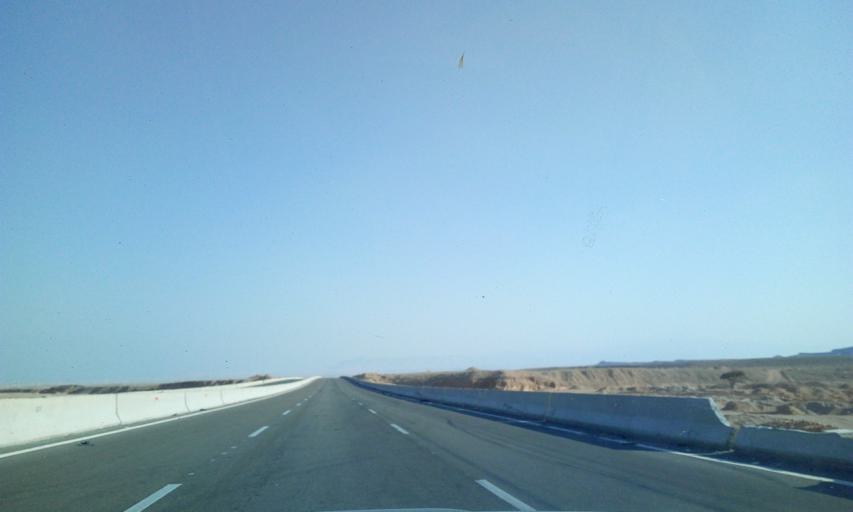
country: EG
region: As Suways
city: Ain Sukhna
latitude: 29.2529
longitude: 32.4774
